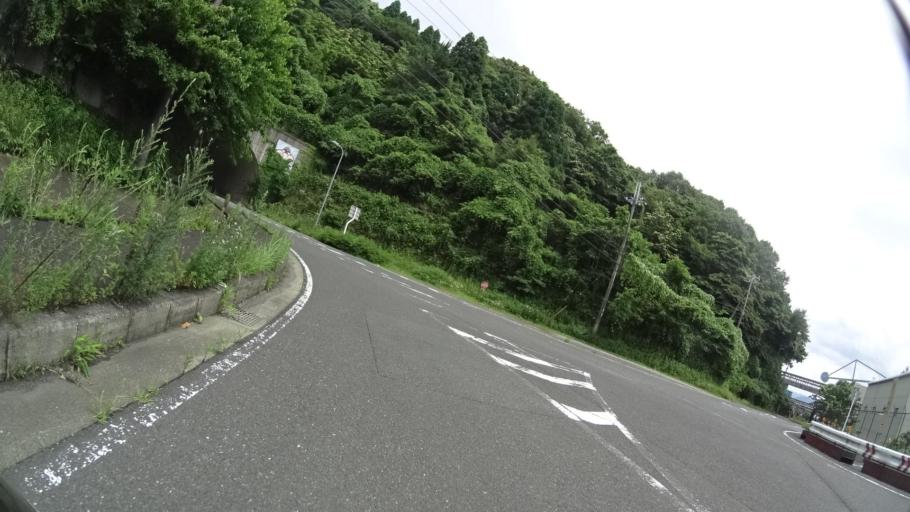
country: JP
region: Kyoto
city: Maizuru
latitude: 35.5238
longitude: 135.3442
